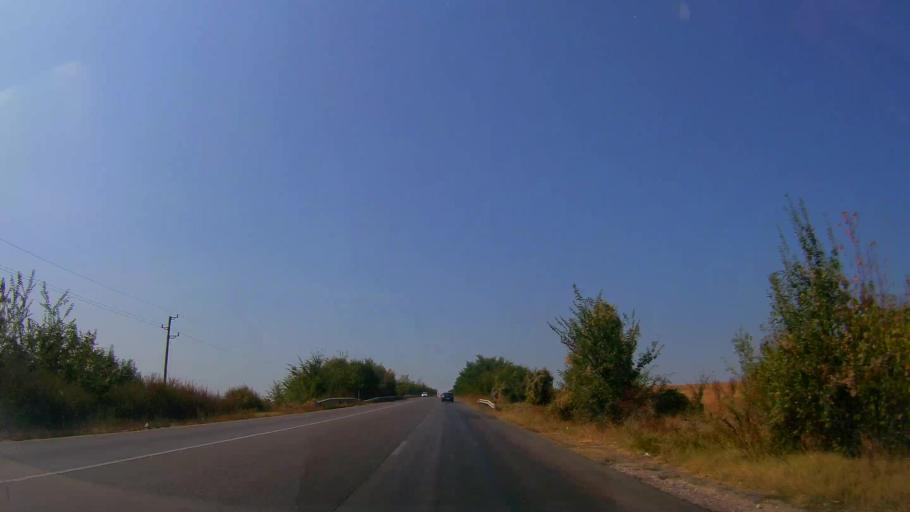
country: BG
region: Ruse
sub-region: Obshtina Vetovo
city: Senovo
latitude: 43.5608
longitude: 26.3706
